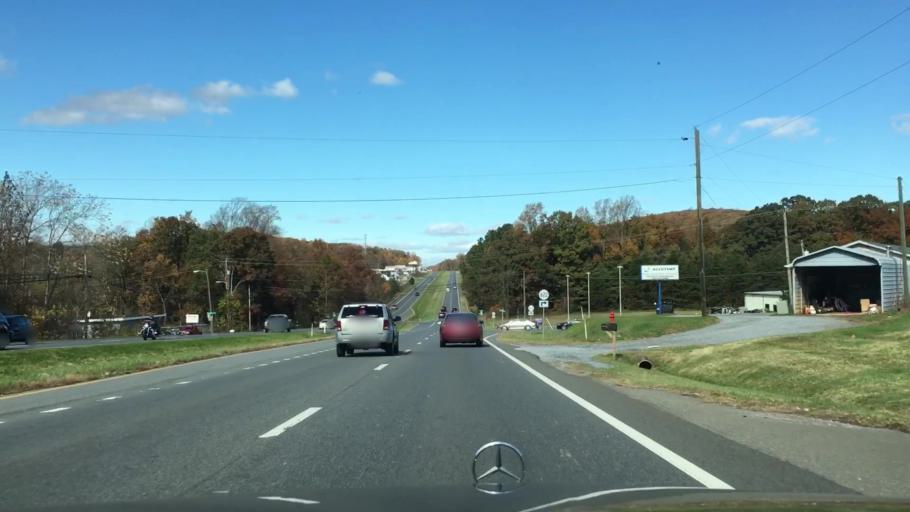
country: US
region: Virginia
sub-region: Campbell County
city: Rustburg
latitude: 37.2876
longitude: -79.1672
